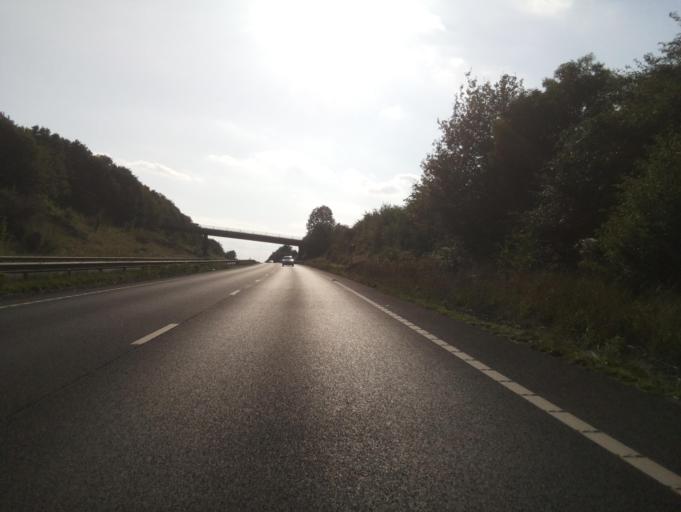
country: GB
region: England
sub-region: Devon
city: Cullompton
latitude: 50.9229
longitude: -3.3955
